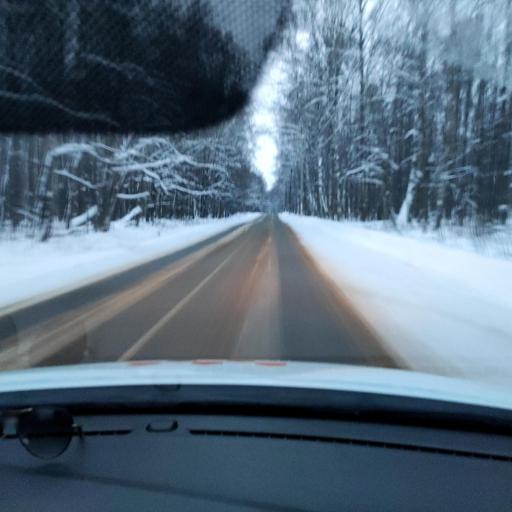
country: RU
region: Tatarstan
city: Vysokaya Gora
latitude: 55.9333
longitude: 49.1831
